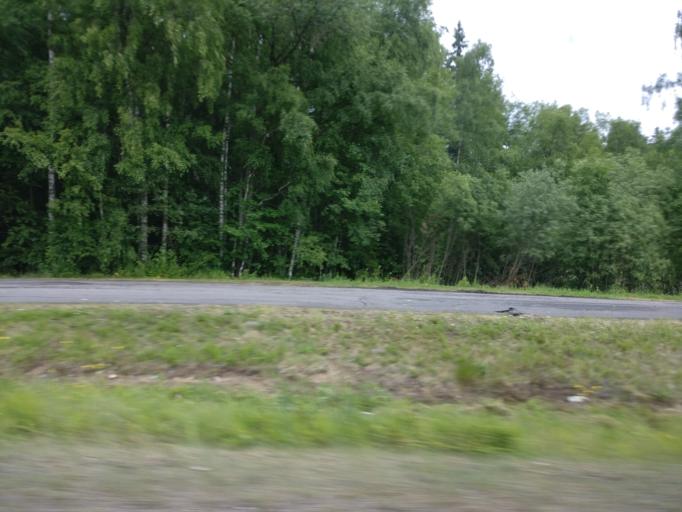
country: FI
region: Southern Savonia
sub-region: Pieksaemaeki
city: Joroinen
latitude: 62.2055
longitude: 27.9646
